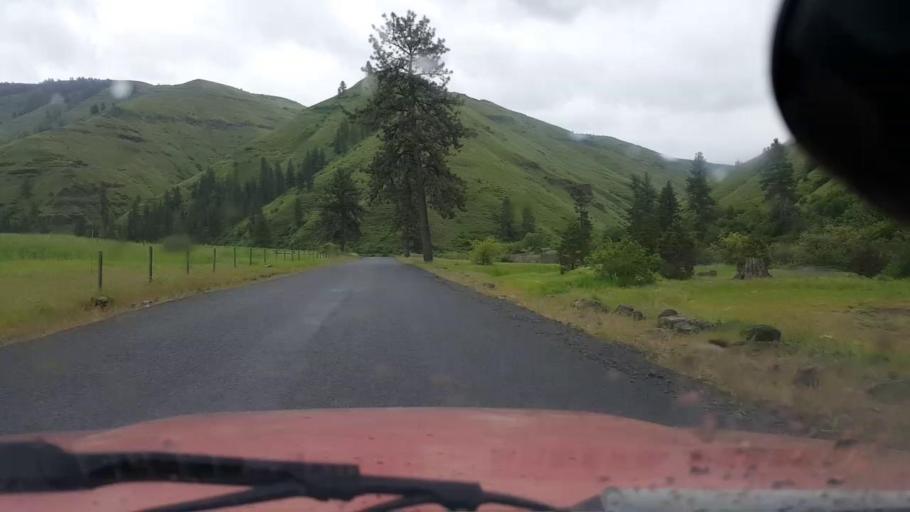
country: US
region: Washington
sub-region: Asotin County
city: Asotin
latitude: 46.0305
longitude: -117.3165
